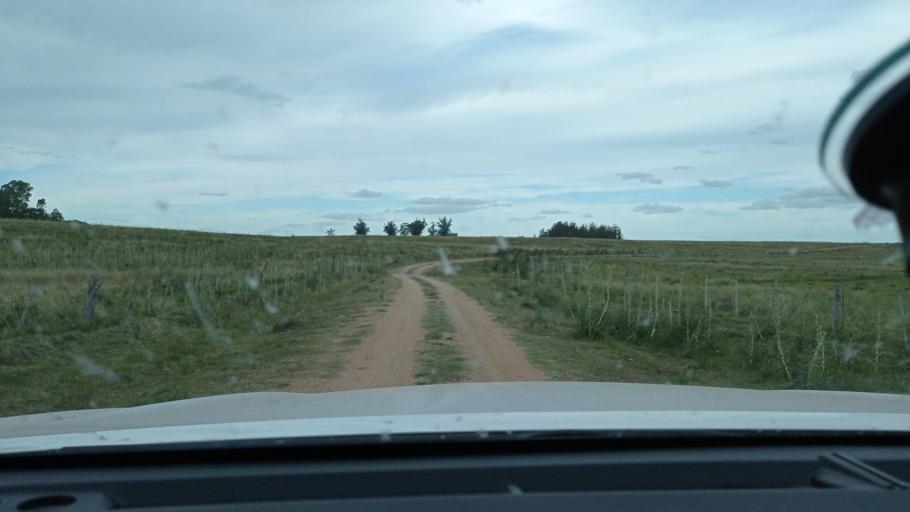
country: UY
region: Florida
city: Casupa
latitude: -34.1247
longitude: -55.8052
